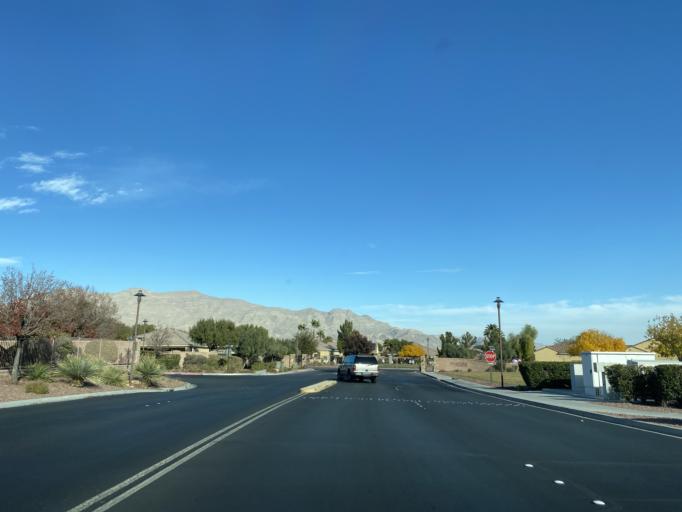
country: US
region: Nevada
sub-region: Clark County
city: North Las Vegas
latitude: 36.3155
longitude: -115.2569
